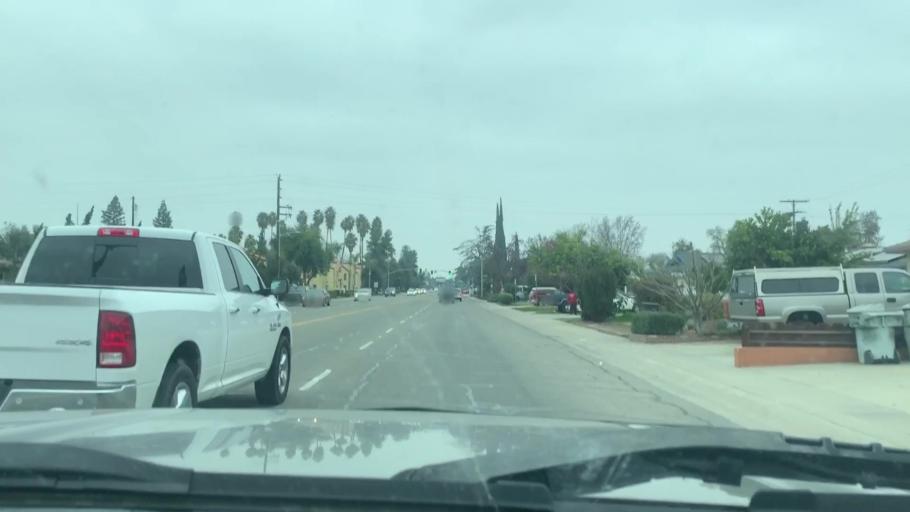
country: US
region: California
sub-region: Tulare County
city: Visalia
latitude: 36.3222
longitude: -119.3317
